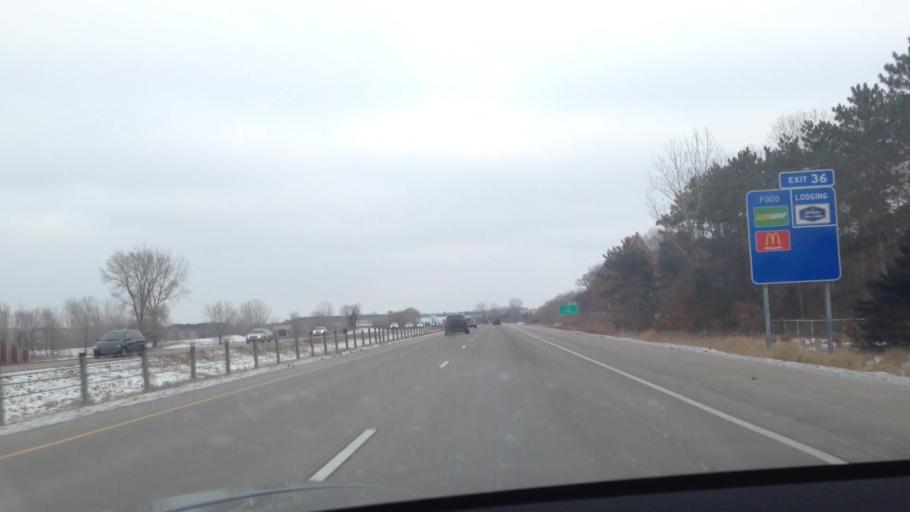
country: US
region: Minnesota
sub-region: Anoka County
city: Circle Pines
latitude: 45.1700
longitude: -93.1346
